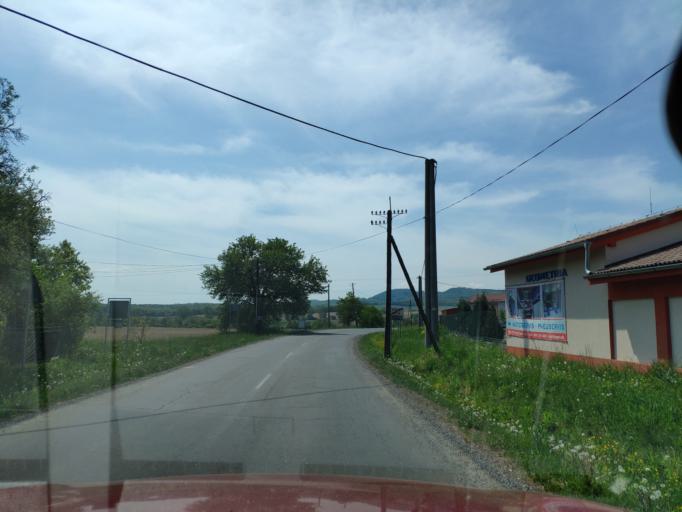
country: SK
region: Banskobystricky
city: Rimavska Sobota
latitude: 48.4681
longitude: 20.0937
